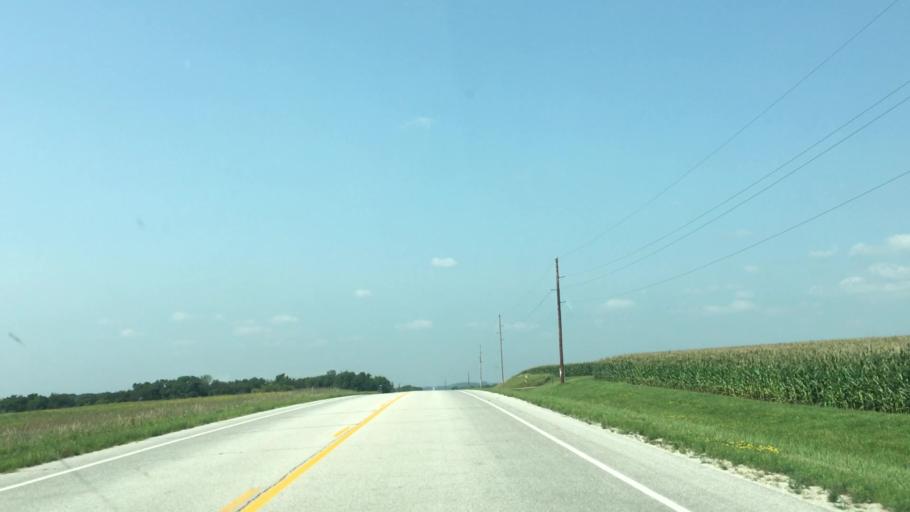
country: US
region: Minnesota
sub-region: Fillmore County
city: Harmony
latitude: 43.5693
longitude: -91.9298
